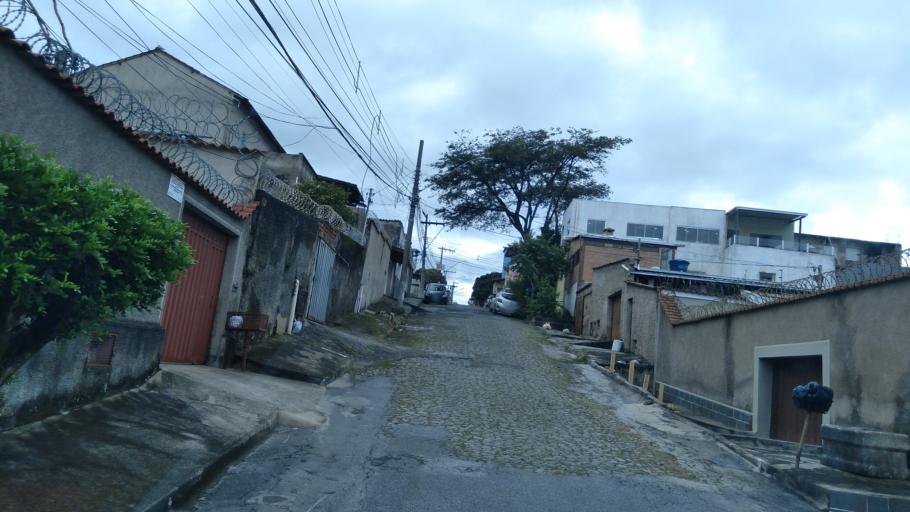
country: BR
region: Minas Gerais
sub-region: Belo Horizonte
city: Belo Horizonte
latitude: -19.9228
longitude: -43.9083
